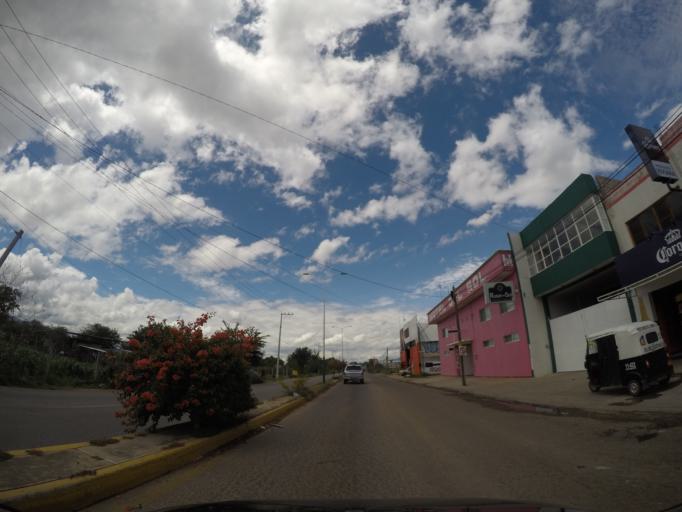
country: MX
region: Oaxaca
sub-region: Santa Cruz Xoxocotlan
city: San Isidro Monjas
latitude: 17.0093
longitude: -96.7362
